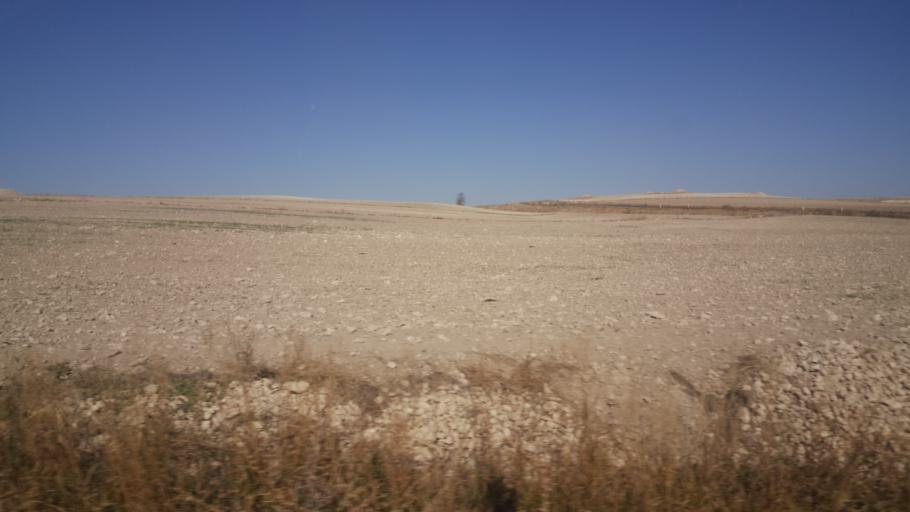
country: TR
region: Konya
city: Celtik
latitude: 39.0741
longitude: 32.0943
